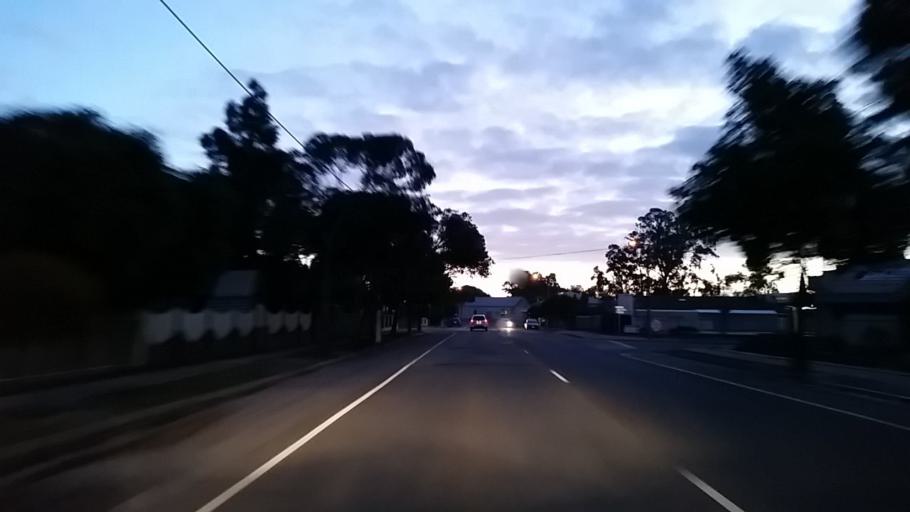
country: AU
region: South Australia
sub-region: Gawler
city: Gawler
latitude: -34.6060
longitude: 138.7422
